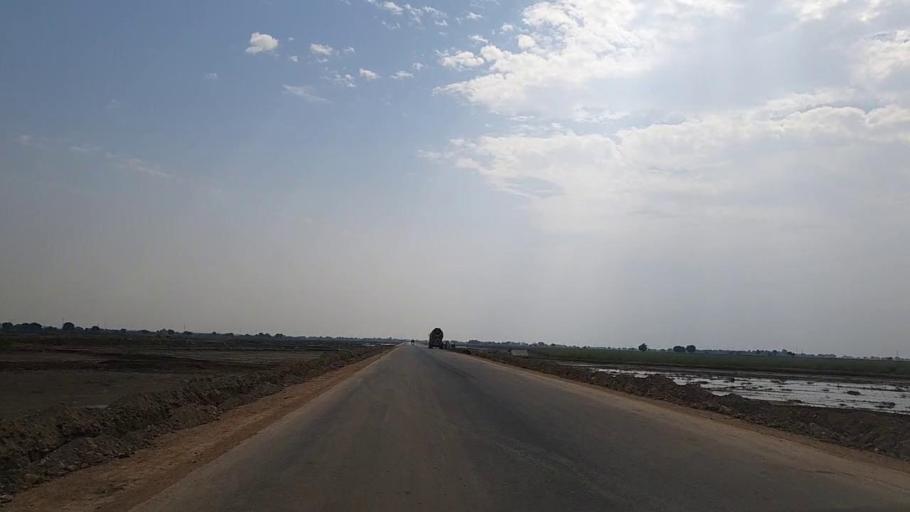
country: PK
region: Sindh
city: Naukot
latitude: 24.9988
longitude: 69.2854
